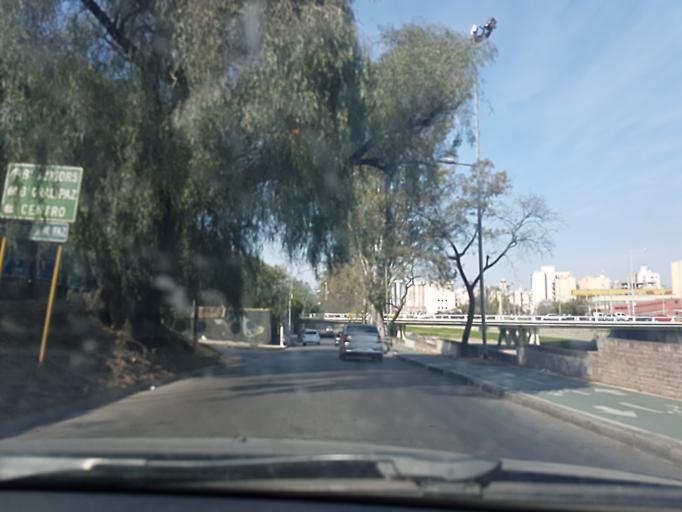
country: AR
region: Cordoba
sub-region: Departamento de Capital
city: Cordoba
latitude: -31.4112
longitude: -64.1745
